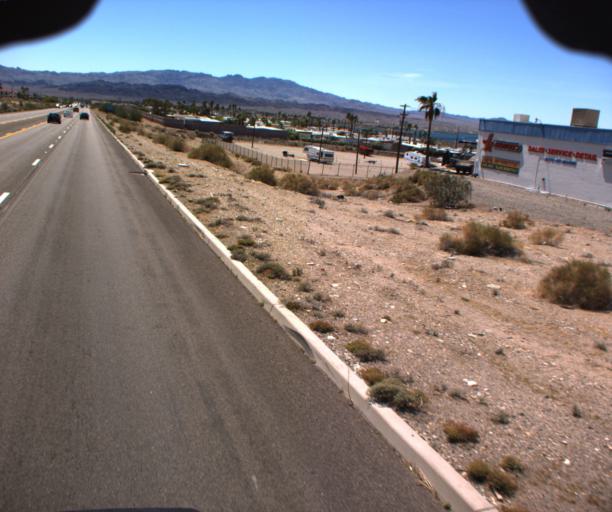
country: US
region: Arizona
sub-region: Mohave County
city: Lake Havasu City
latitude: 34.4903
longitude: -114.3494
